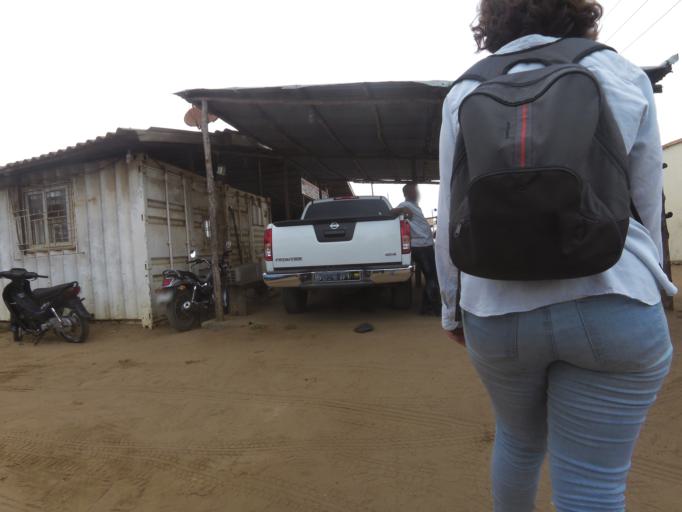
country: BJ
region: Queme
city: Porto-Novo
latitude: 6.3808
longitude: 2.7036
